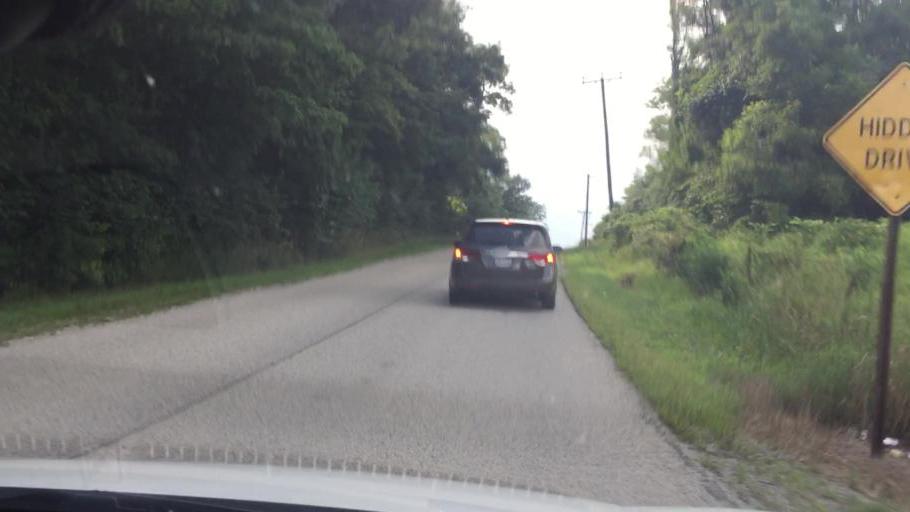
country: US
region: Ohio
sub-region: Clark County
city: Lisbon
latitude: 39.9447
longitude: -83.5947
